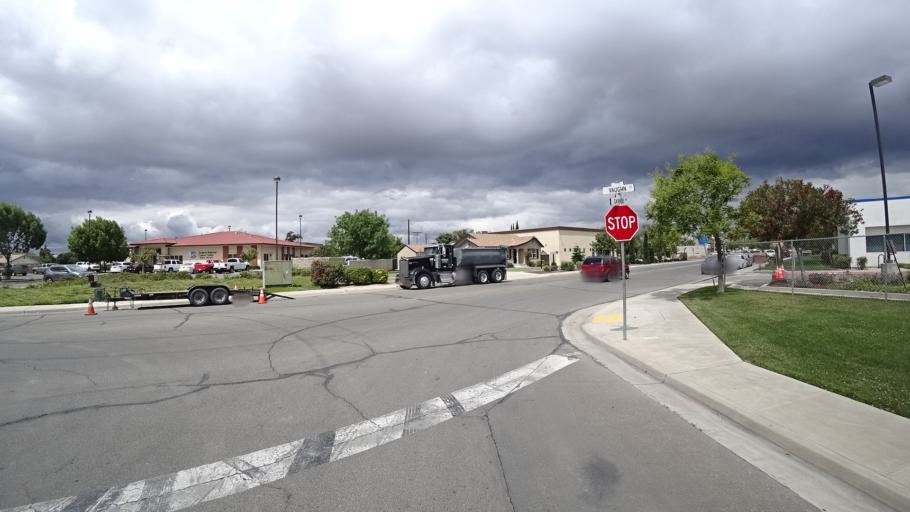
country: US
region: California
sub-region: Kings County
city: Hanford
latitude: 36.3263
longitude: -119.6574
